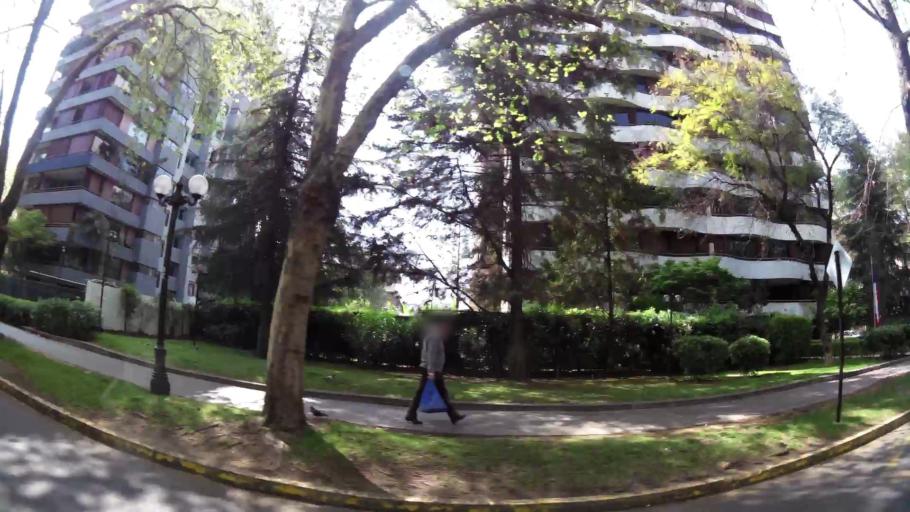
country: CL
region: Santiago Metropolitan
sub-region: Provincia de Santiago
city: Villa Presidente Frei, Nunoa, Santiago, Chile
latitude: -33.4233
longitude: -70.5979
